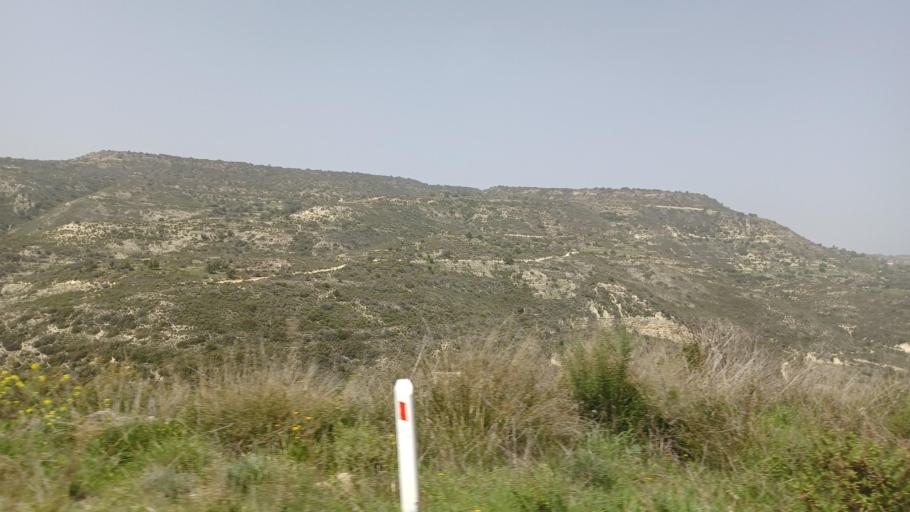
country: CY
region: Limassol
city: Pachna
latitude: 34.7590
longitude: 32.7439
